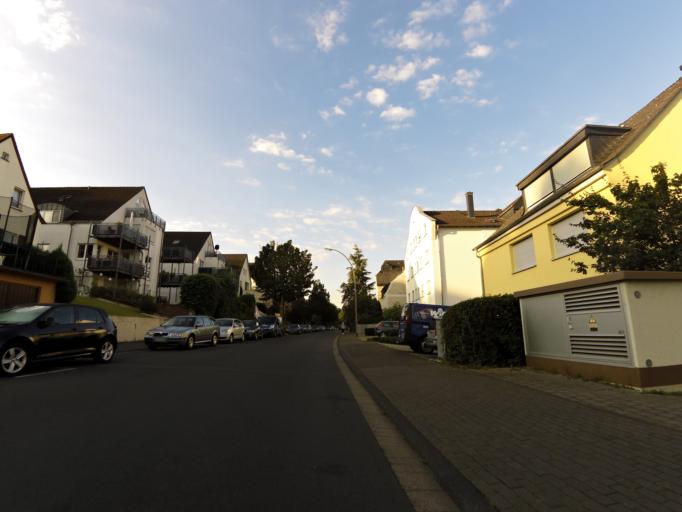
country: DE
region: Rheinland-Pfalz
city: Koblenz
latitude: 50.3361
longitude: 7.5991
